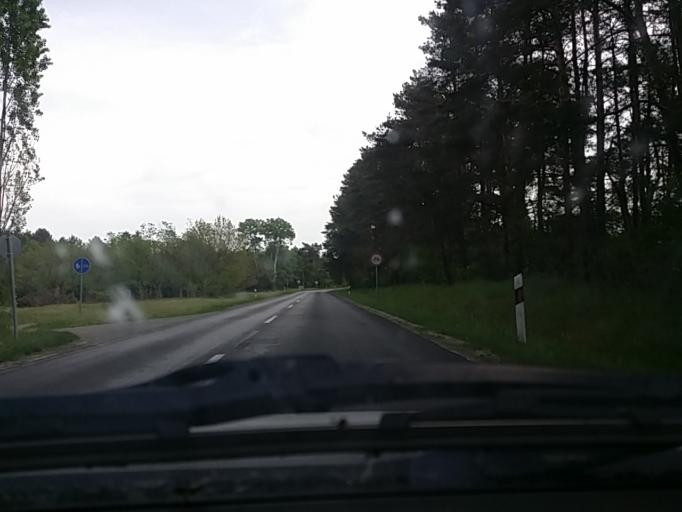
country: HU
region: Somogy
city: Barcs
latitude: 45.9795
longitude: 17.5766
